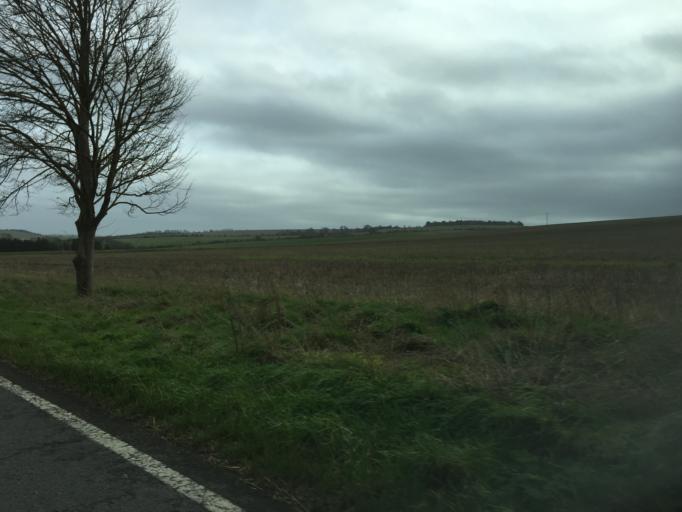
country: GB
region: England
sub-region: Oxfordshire
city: Blewbury
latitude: 51.5709
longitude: -1.2519
